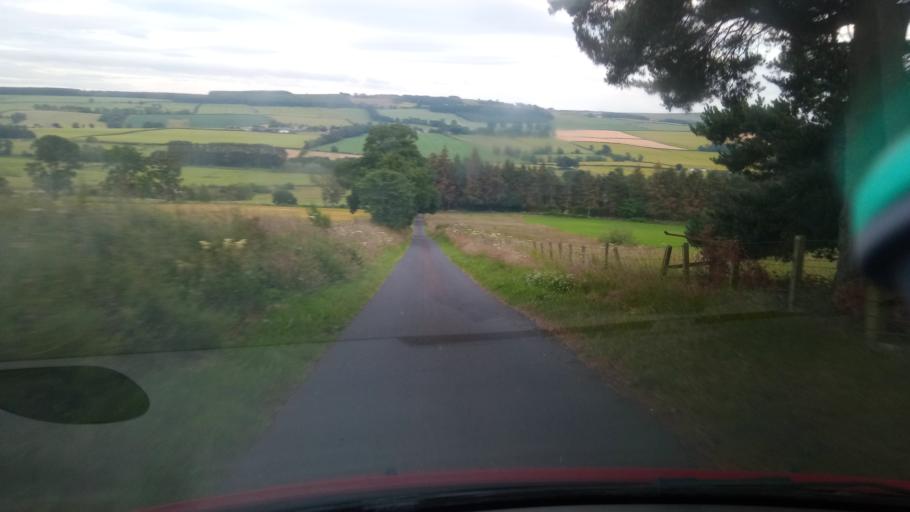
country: GB
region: Scotland
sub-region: The Scottish Borders
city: Jedburgh
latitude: 55.5006
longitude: -2.6217
